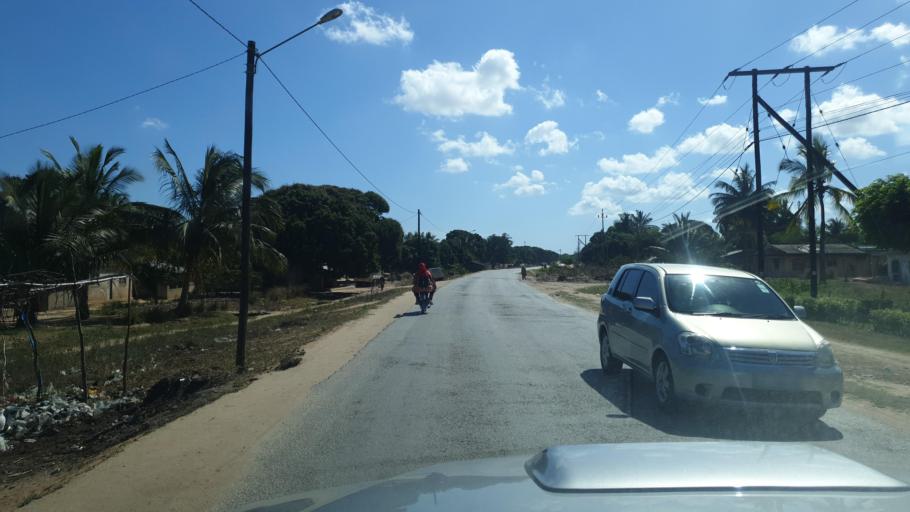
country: MZ
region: Nampula
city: Nacala
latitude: -14.5194
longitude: 40.6956
